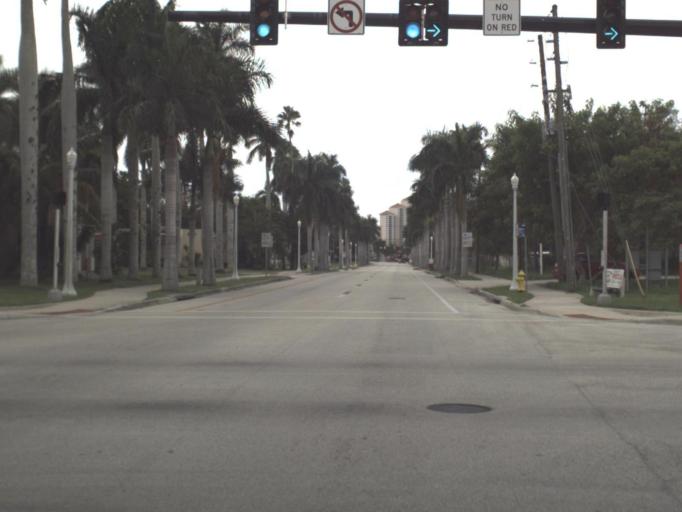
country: US
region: Florida
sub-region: Lee County
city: North Fort Myers
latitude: 26.6484
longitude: -81.8627
